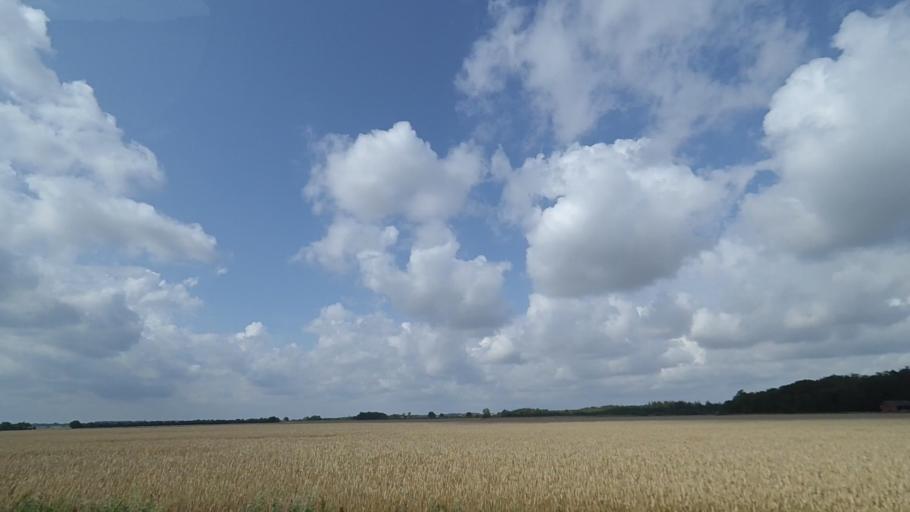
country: DK
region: Central Jutland
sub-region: Norddjurs Kommune
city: Auning
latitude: 56.5088
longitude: 10.4205
